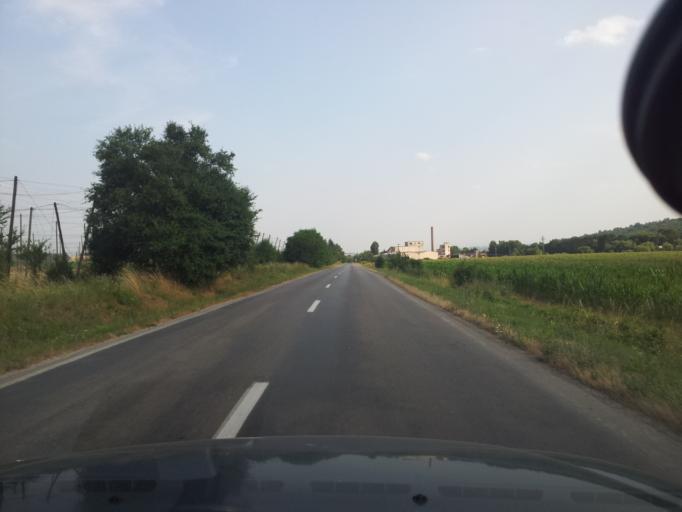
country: SK
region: Nitriansky
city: Trencianske Teplice
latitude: 48.8137
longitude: 18.1842
